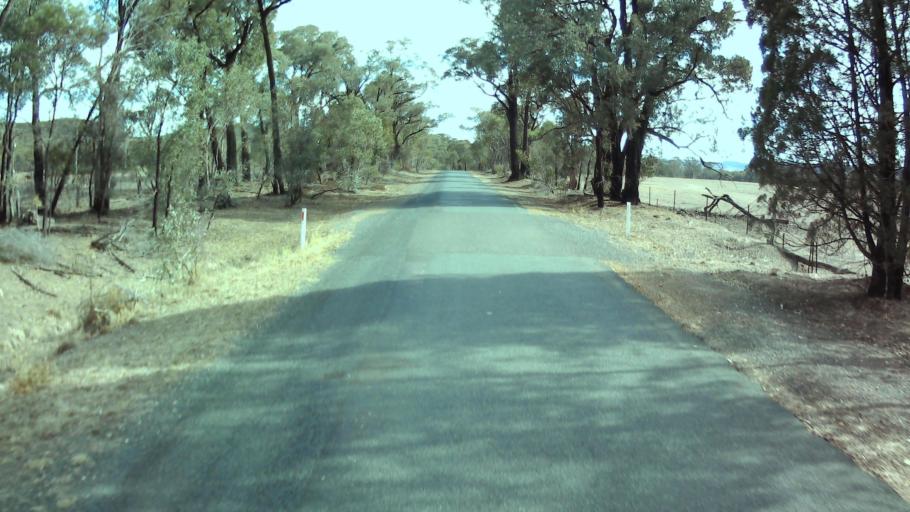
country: AU
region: New South Wales
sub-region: Weddin
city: Grenfell
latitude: -33.8751
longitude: 148.2016
